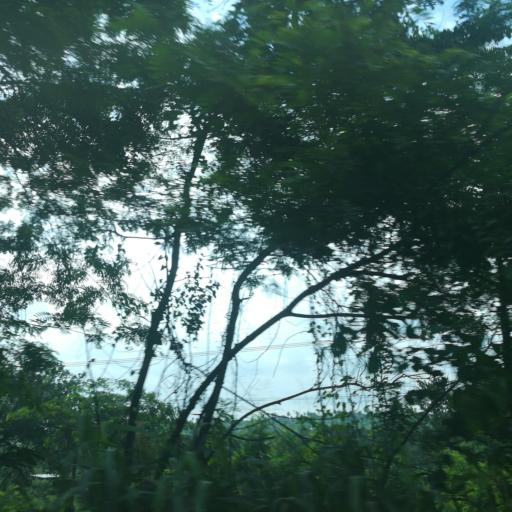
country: NG
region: Lagos
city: Ikorodu
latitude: 6.6634
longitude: 3.6342
